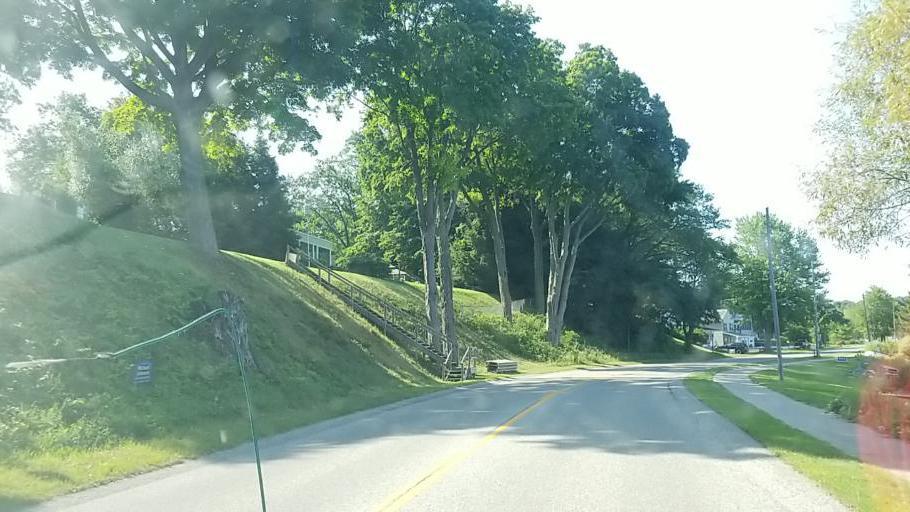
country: US
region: Michigan
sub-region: Muskegon County
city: Whitehall
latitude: 43.3922
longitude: -86.3535
